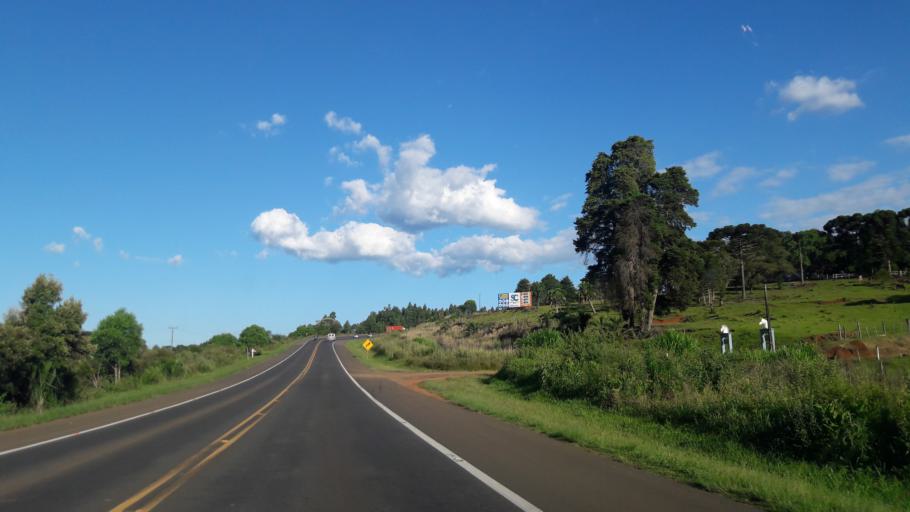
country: BR
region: Parana
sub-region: Guarapuava
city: Guarapuava
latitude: -25.3659
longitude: -51.3451
